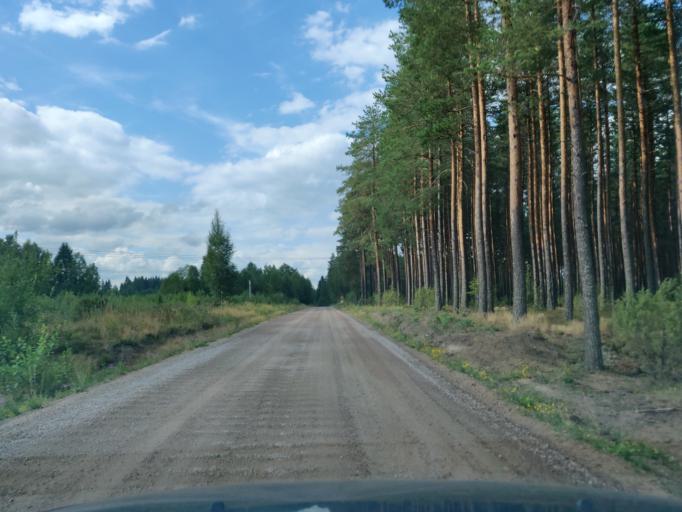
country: SE
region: Vaermland
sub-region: Munkfors Kommun
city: Munkfors
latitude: 59.9762
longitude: 13.5345
